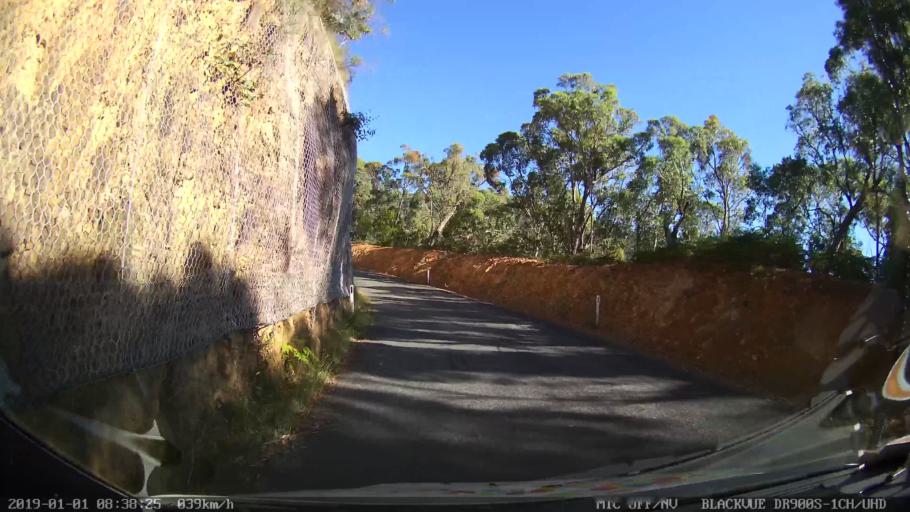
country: AU
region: New South Wales
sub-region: Snowy River
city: Jindabyne
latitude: -36.3323
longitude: 148.1980
